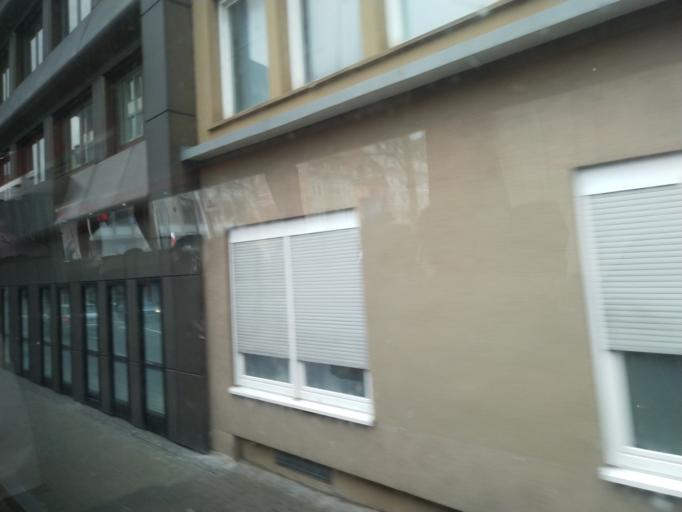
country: DE
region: Saarland
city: Saarbrucken
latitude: 49.2369
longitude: 6.9967
